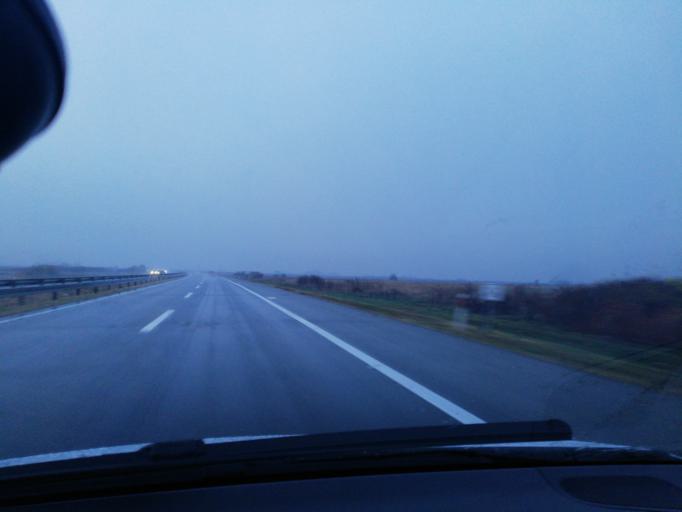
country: RS
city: Sasinci
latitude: 44.9947
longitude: 19.6981
